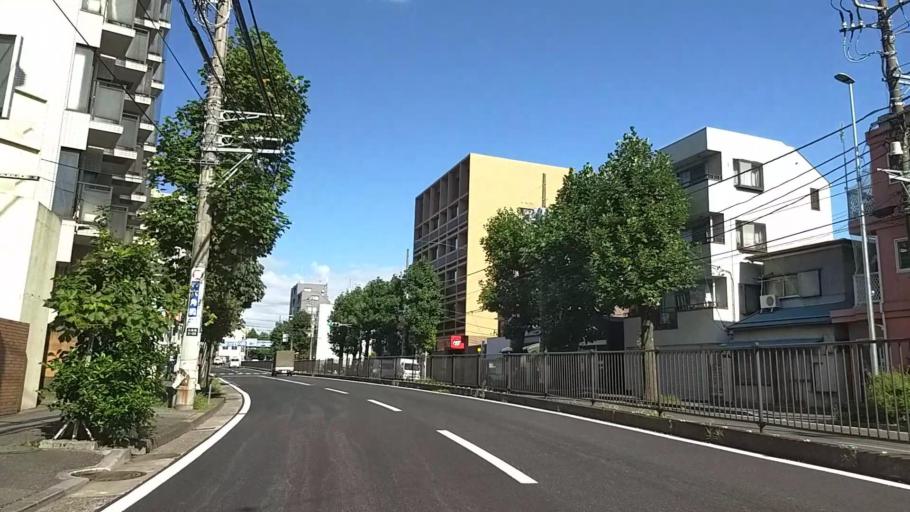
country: JP
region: Kanagawa
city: Yokohama
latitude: 35.4894
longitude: 139.6232
